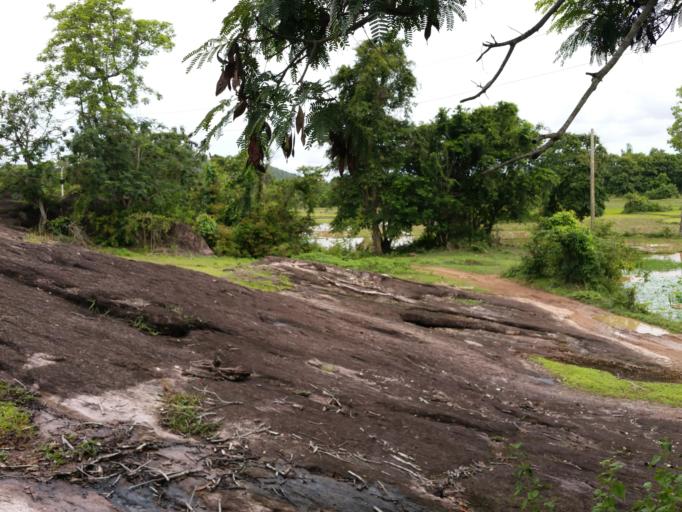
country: LA
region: Champasak
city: Khong
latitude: 14.1560
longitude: 105.7919
